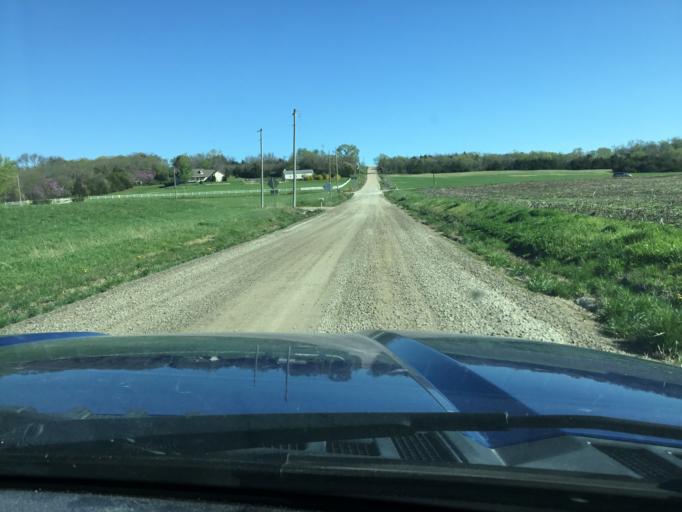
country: US
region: Kansas
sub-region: Douglas County
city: Lawrence
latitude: 38.9917
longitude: -95.3165
